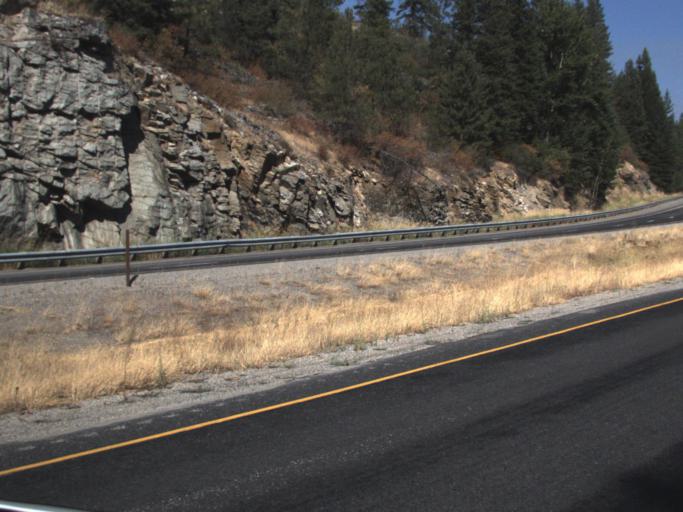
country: US
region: Washington
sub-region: Spokane County
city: Deer Park
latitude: 48.0945
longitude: -117.3181
